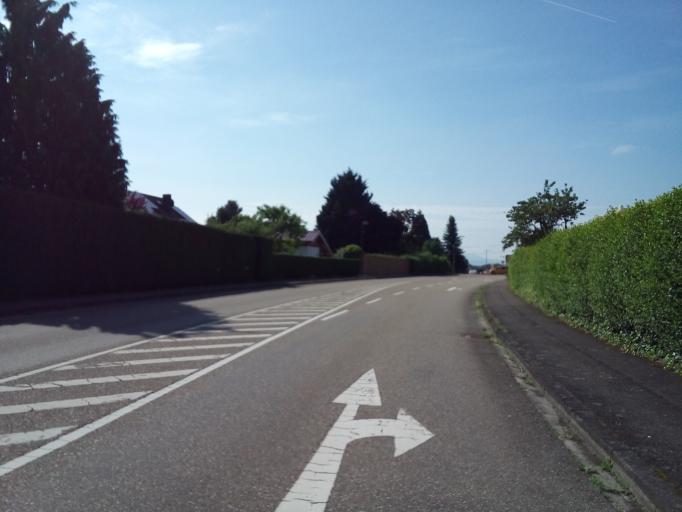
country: DE
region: Baden-Wuerttemberg
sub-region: Freiburg Region
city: Rheinau
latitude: 48.6513
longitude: 7.9336
